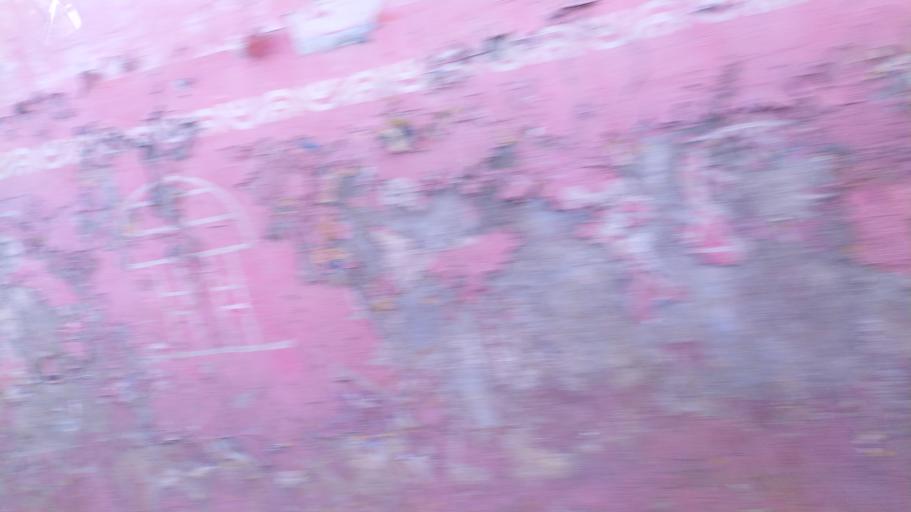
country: IN
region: Telangana
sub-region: Hyderabad
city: Hyderabad
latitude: 17.3208
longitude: 78.4332
